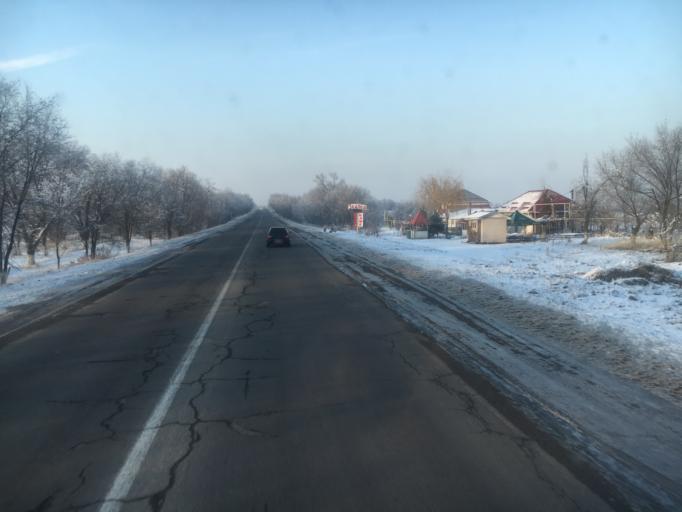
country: KZ
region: Almaty Oblysy
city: Burunday
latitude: 43.3108
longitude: 76.6660
